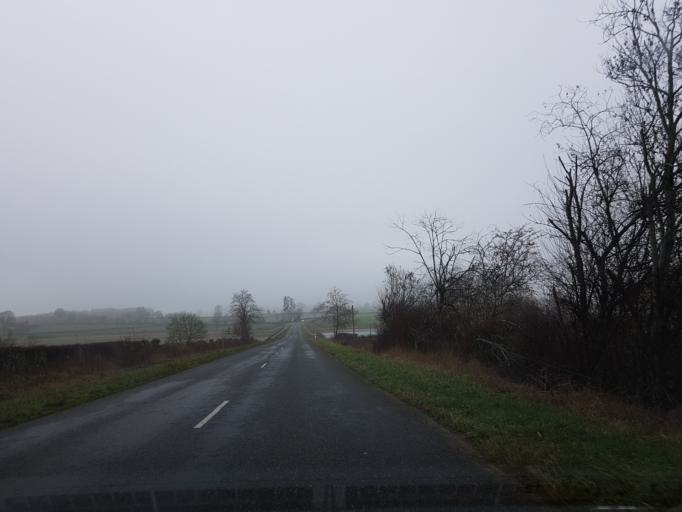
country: FR
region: Bourgogne
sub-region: Departement de Saone-et-Loire
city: Blanzy
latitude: 46.7356
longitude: 4.3456
